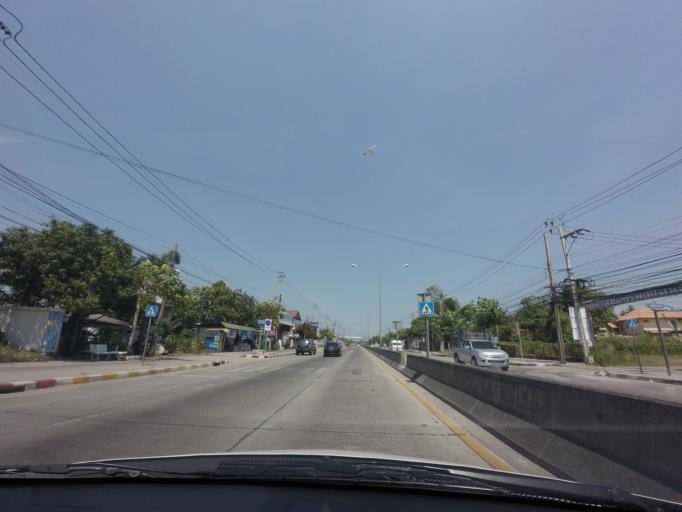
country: TH
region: Bangkok
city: Khlong Sam Wa
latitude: 13.8310
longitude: 100.7710
